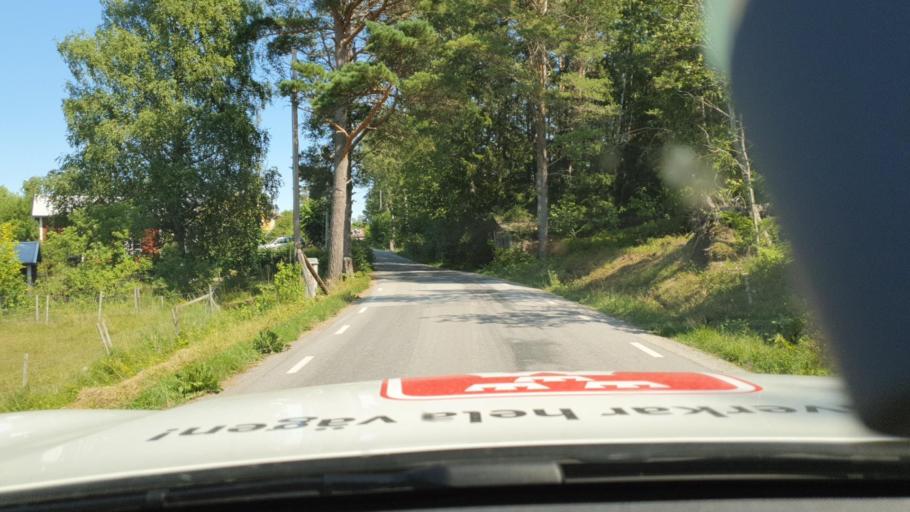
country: SE
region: Stockholm
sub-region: Norrtalje Kommun
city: Bjorko
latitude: 59.8130
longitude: 18.9782
